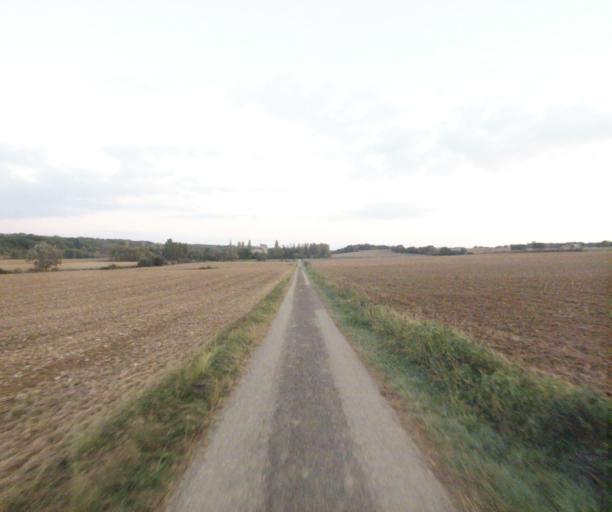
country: FR
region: Midi-Pyrenees
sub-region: Departement du Gers
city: Vic-Fezensac
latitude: 43.8128
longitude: 0.2530
